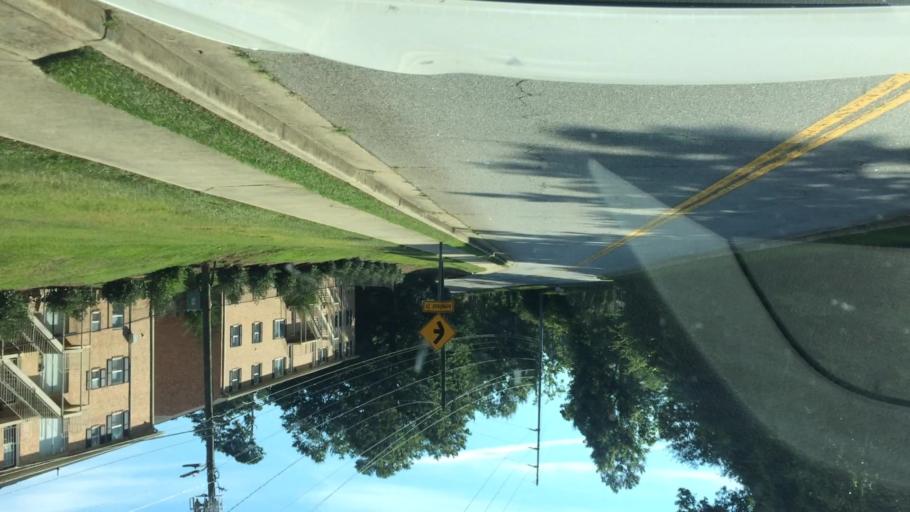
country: US
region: Georgia
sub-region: Columbia County
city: Martinez
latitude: 33.5044
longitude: -82.0400
